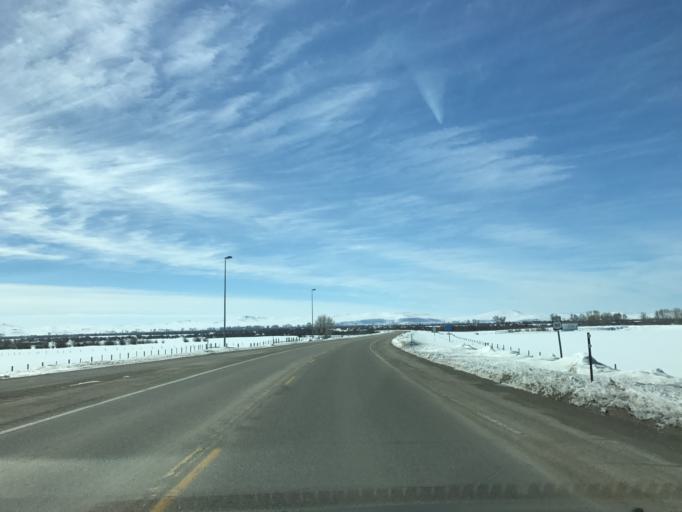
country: US
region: Wyoming
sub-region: Sublette County
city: Pinedale
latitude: 42.8897
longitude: -110.0697
